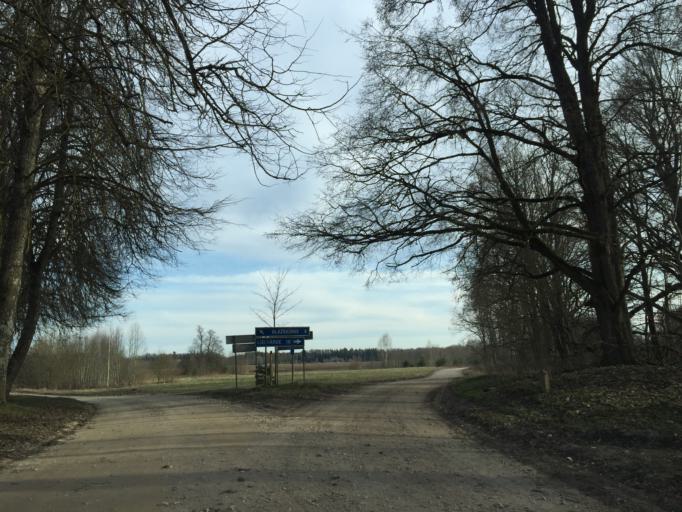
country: LV
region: Kegums
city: Kegums
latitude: 56.7988
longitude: 24.7491
